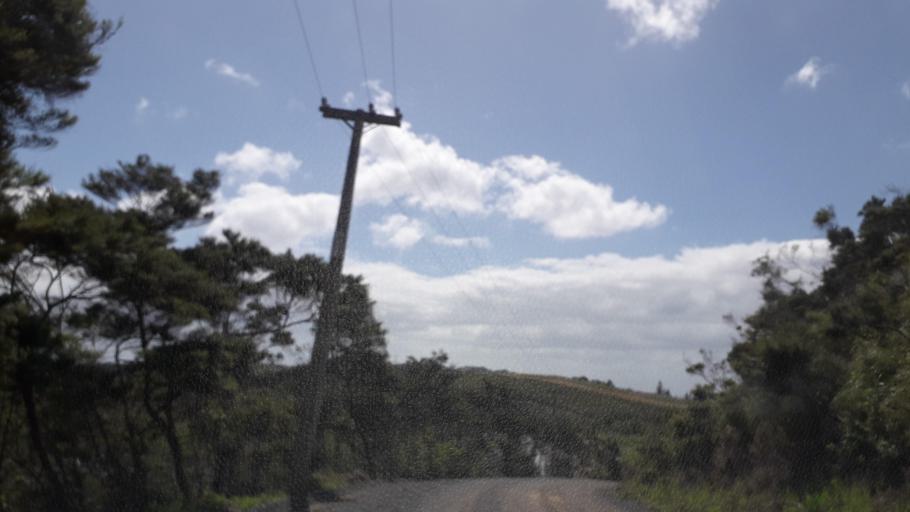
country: NZ
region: Northland
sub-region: Far North District
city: Paihia
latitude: -35.2424
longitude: 174.2480
